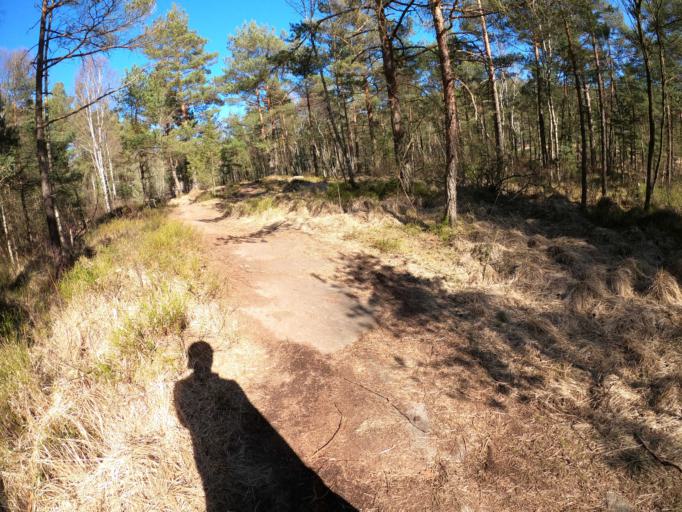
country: SE
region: Vaestra Goetaland
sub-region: Harryda Kommun
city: Molnlycke
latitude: 57.6403
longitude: 12.1148
